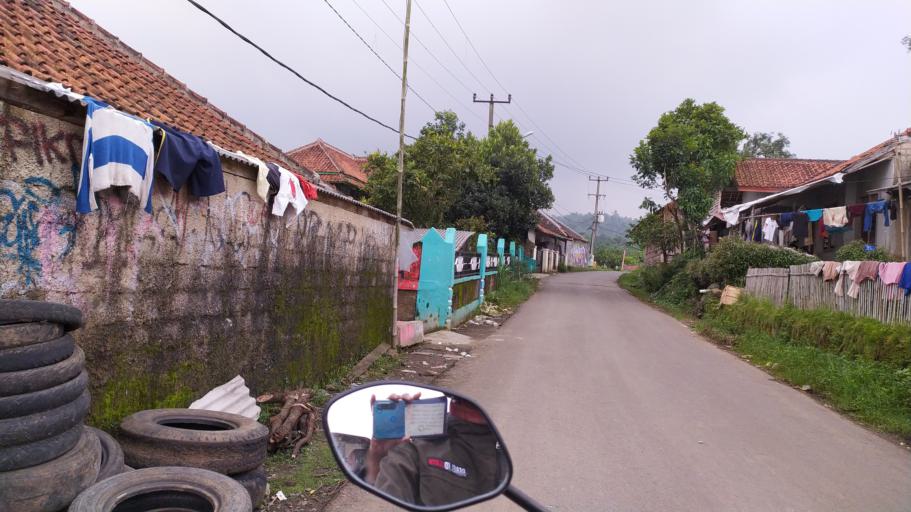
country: ID
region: West Java
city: Ciampea
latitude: -6.6402
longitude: 106.7073
